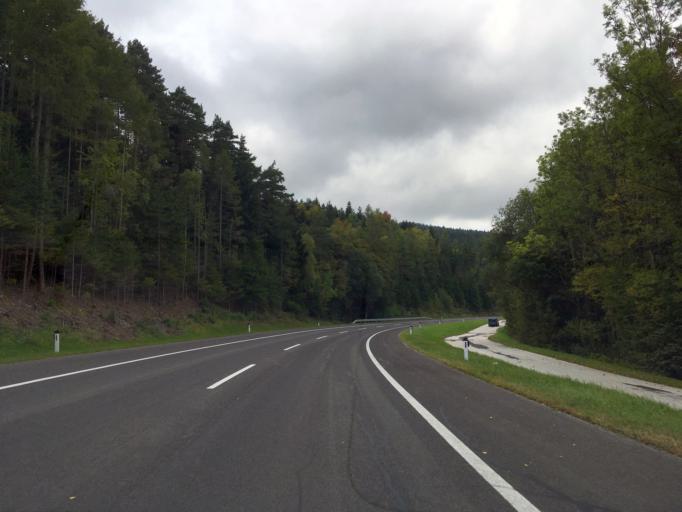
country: AT
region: Lower Austria
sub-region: Politischer Bezirk Neunkirchen
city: Monichkirchen
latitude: 47.5035
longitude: 16.0311
